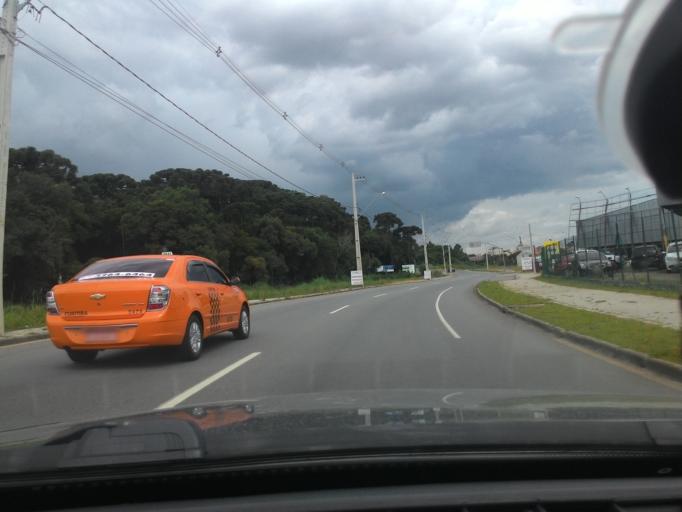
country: BR
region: Parana
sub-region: Sao Jose Dos Pinhais
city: Sao Jose dos Pinhais
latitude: -25.5354
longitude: -49.1888
